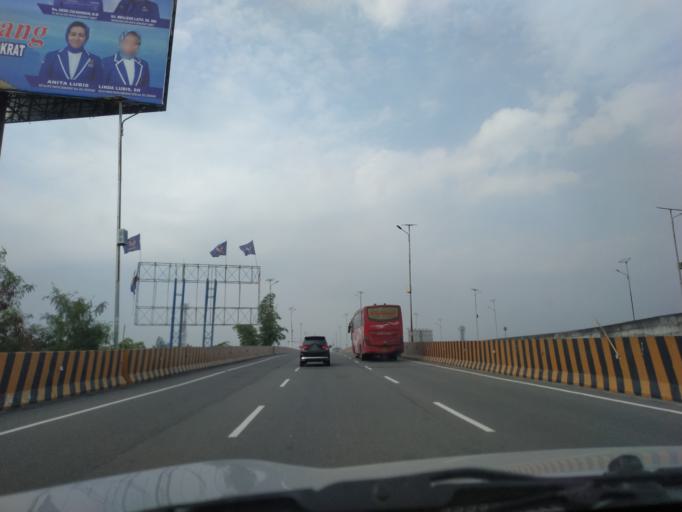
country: ID
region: North Sumatra
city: Percut
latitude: 3.6105
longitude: 98.8544
